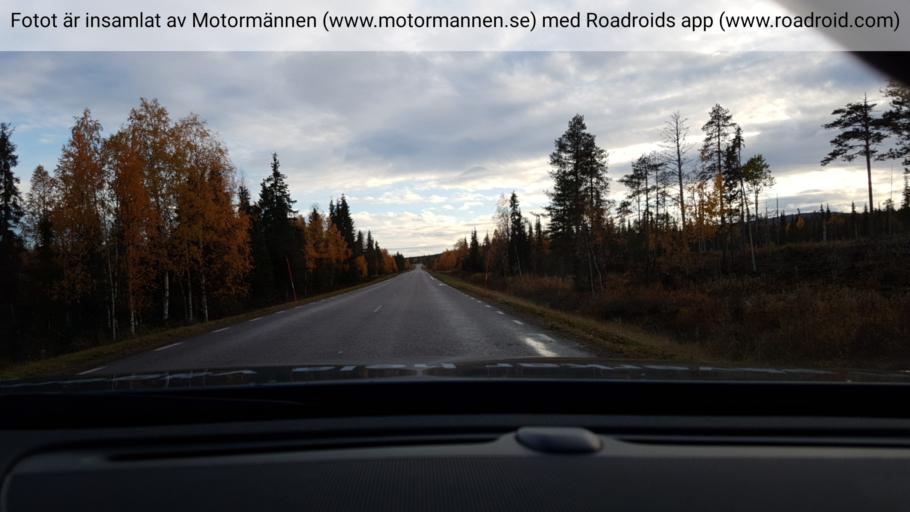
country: SE
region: Norrbotten
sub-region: Overkalix Kommun
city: OEverkalix
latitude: 66.8764
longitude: 22.7616
